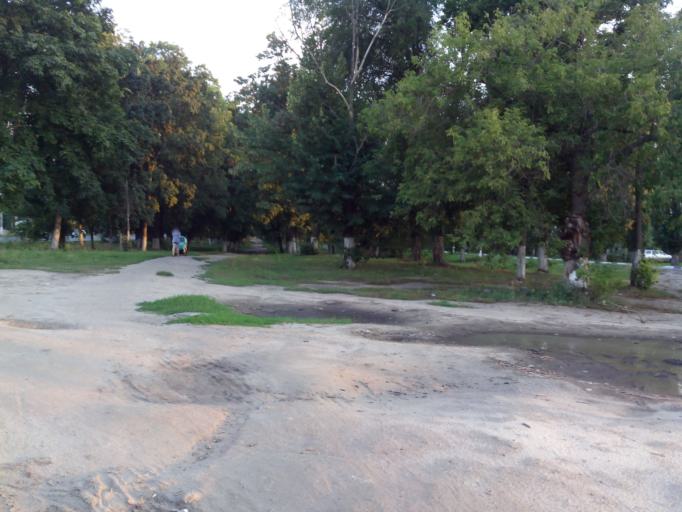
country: RU
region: Voronezj
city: Borisoglebsk
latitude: 51.3595
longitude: 42.0760
